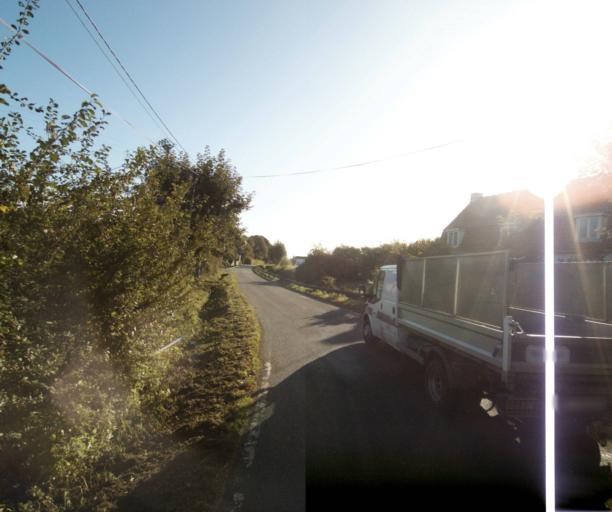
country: FR
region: Nord-Pas-de-Calais
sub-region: Departement du Nord
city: Verlinghem
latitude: 50.6719
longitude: 3.0059
